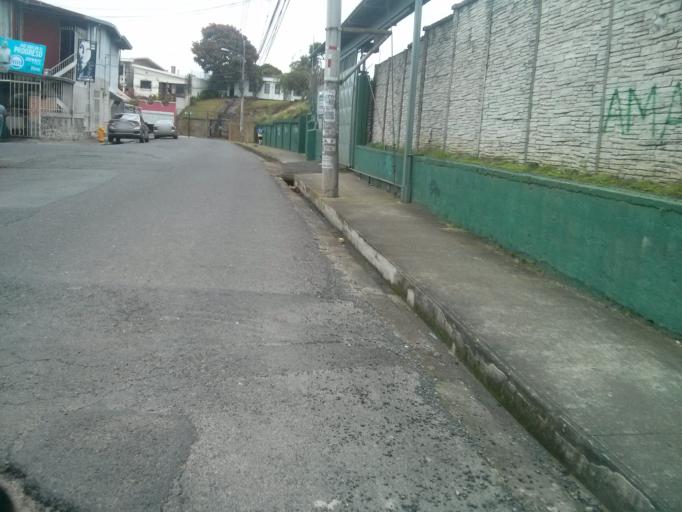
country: CR
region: San Jose
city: San Pedro
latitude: 9.9243
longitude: -84.0535
